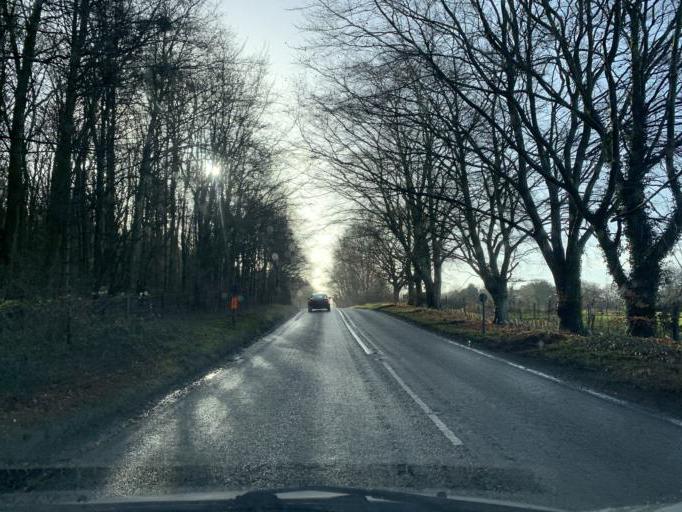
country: GB
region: England
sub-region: Wiltshire
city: Winterbourne Stoke
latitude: 51.1533
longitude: -1.8591
